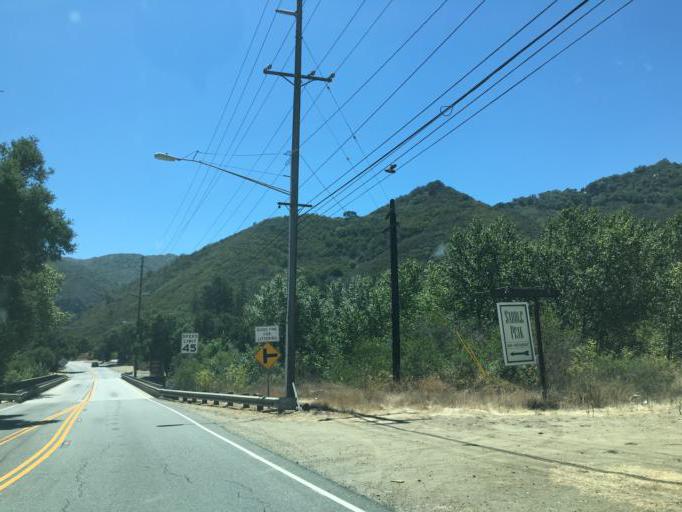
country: US
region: California
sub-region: Los Angeles County
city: Malibu Beach
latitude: 34.0821
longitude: -118.7046
